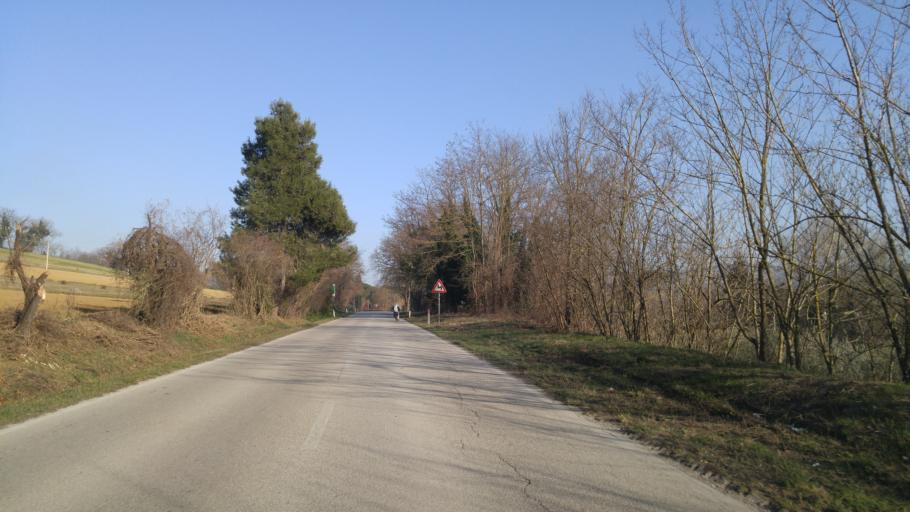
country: IT
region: The Marches
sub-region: Provincia di Pesaro e Urbino
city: Fenile
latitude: 43.8366
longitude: 12.9383
